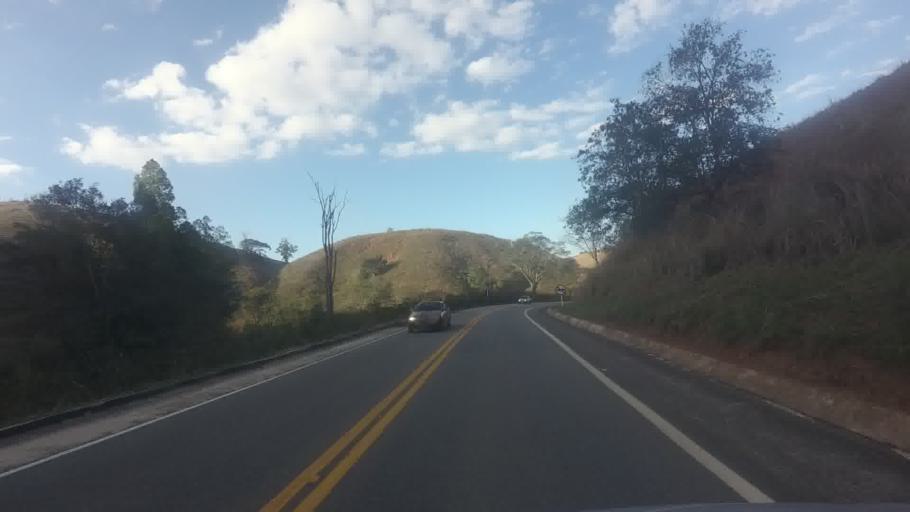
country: BR
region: Espirito Santo
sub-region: Mimoso Do Sul
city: Mimoso do Sul
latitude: -20.9242
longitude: -41.3168
